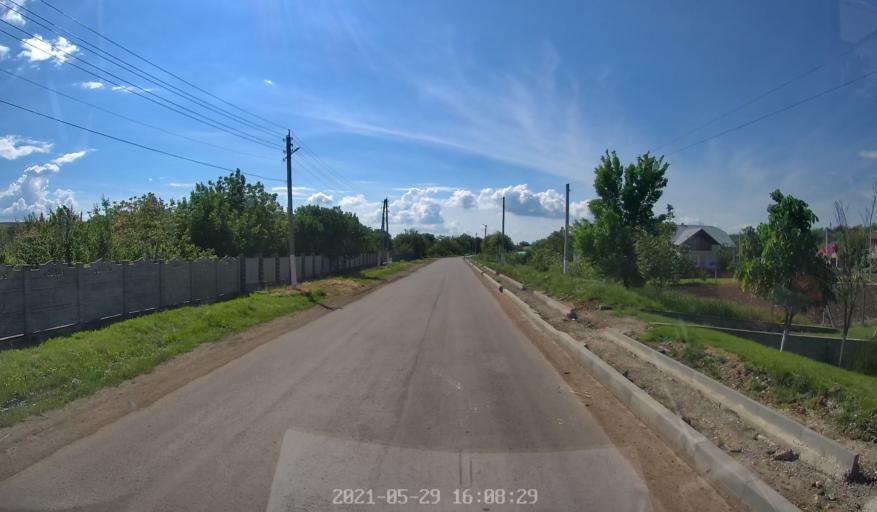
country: MD
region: Chisinau
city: Singera
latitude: 46.8182
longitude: 28.8908
